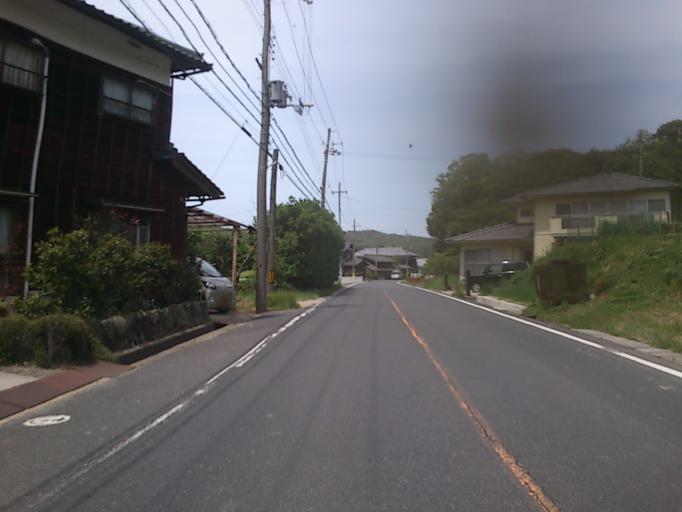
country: JP
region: Kyoto
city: Miyazu
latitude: 35.6863
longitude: 135.0983
